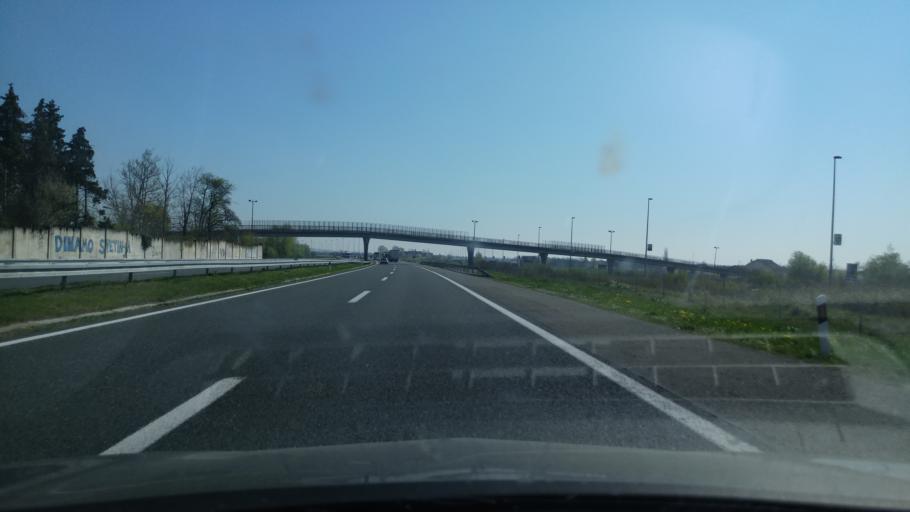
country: HR
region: Brodsko-Posavska
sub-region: Grad Slavonski Brod
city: Slavonski Brod
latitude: 45.1794
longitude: 17.9959
